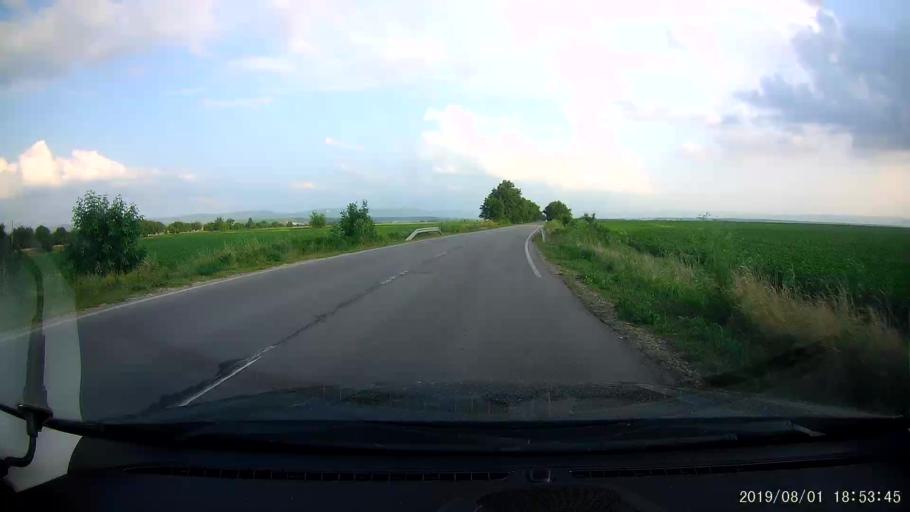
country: BG
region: Shumen
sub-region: Obshtina Shumen
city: Shumen
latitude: 43.2154
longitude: 26.9975
